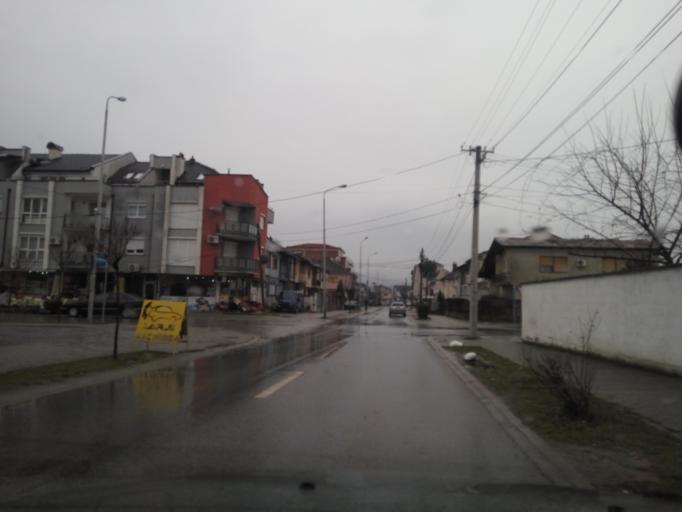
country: XK
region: Gjakova
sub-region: Komuna e Gjakoves
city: Gjakove
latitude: 42.3733
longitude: 20.4405
